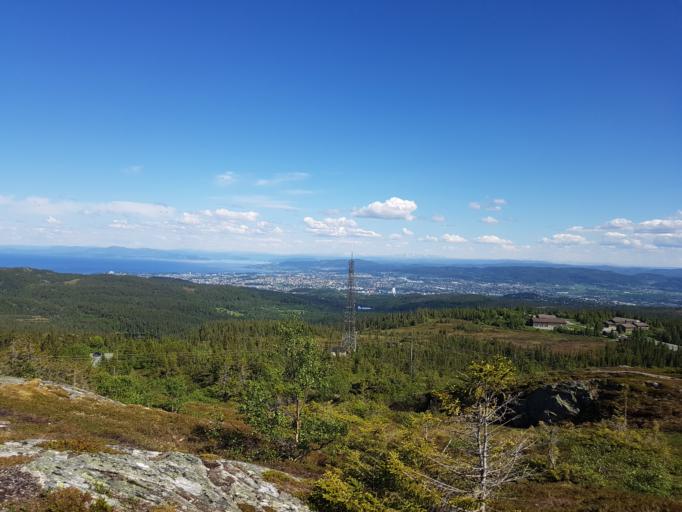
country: NO
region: Sor-Trondelag
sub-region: Melhus
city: Melhus
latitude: 63.4213
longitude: 10.2545
